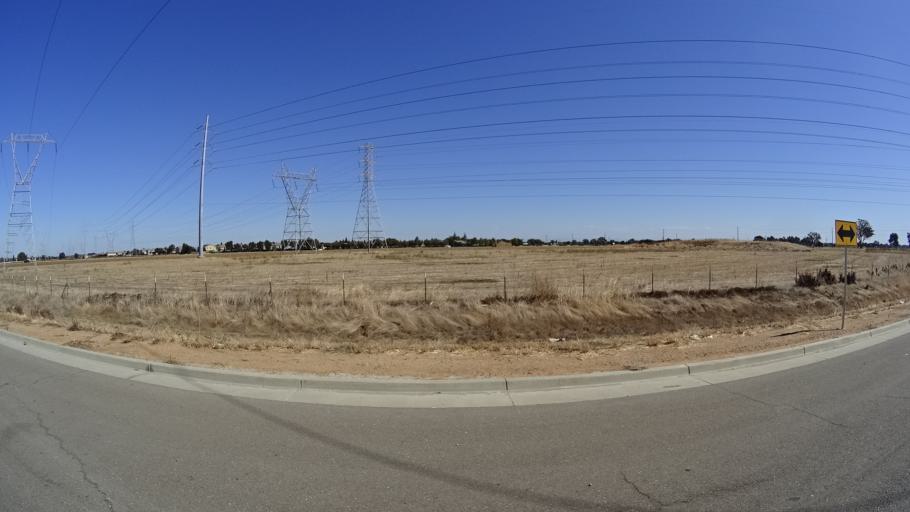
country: US
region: California
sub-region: Sacramento County
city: Elk Grove
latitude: 38.3871
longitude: -121.3524
